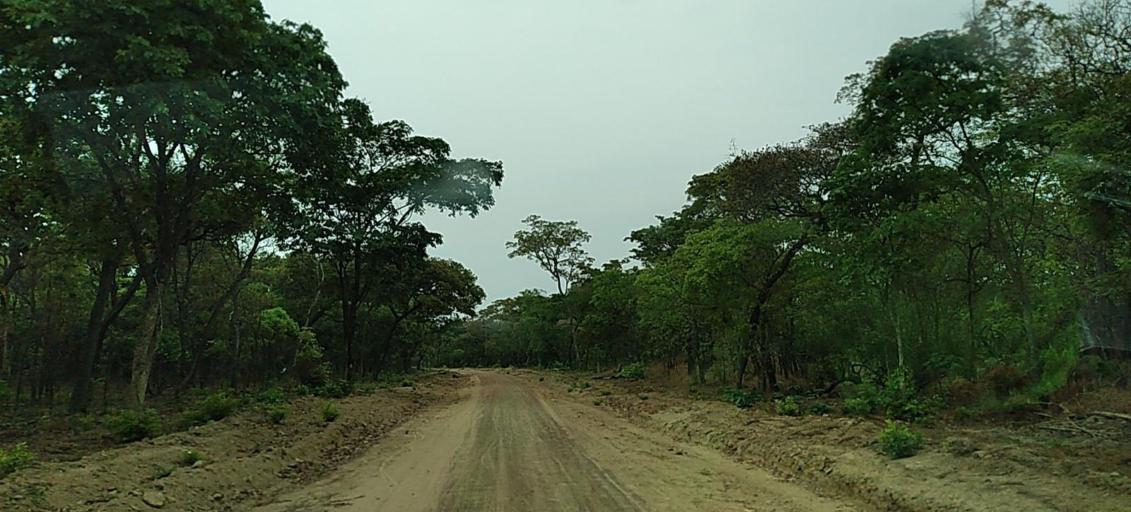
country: ZM
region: North-Western
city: Solwezi
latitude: -12.5201
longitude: 26.5242
